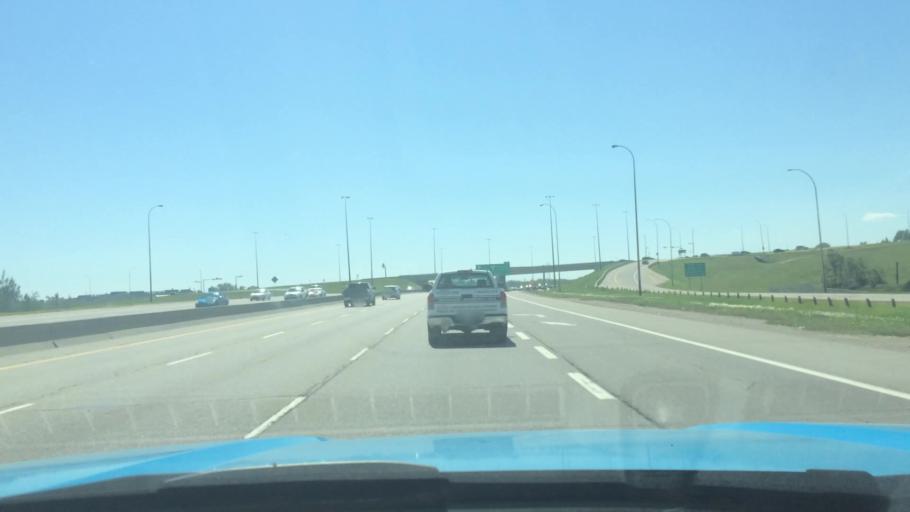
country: CA
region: Alberta
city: Calgary
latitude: 50.9705
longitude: -114.0366
